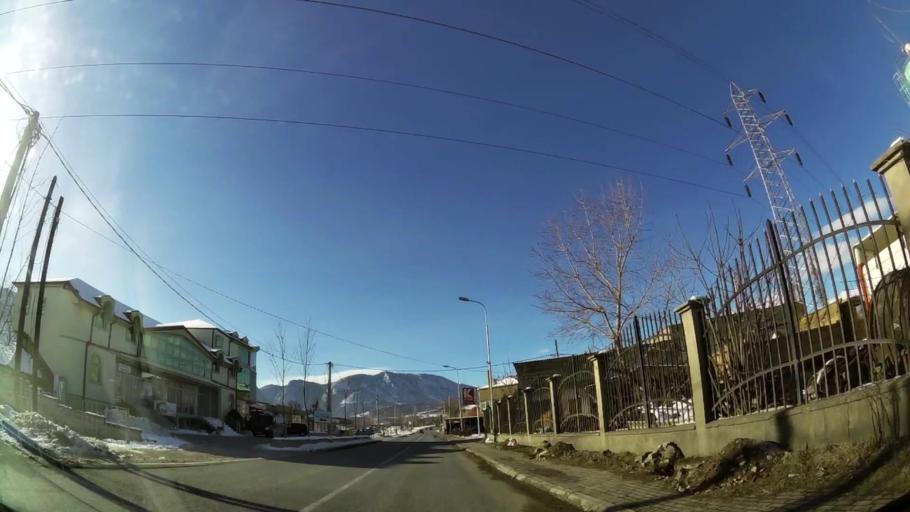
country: MK
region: Saraj
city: Saraj
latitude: 41.9955
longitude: 21.3225
